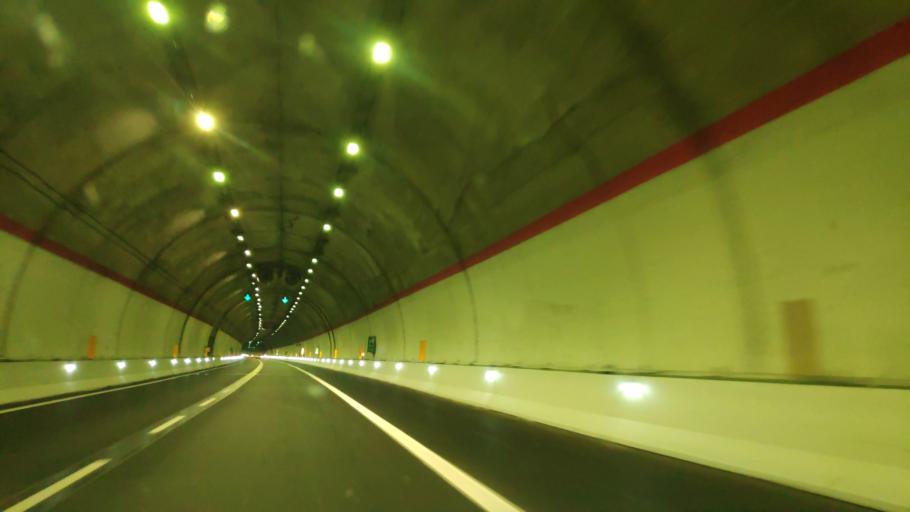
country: IT
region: Calabria
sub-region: Provincia di Reggio Calabria
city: Bagnara Calabra
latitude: 38.2560
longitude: 15.7710
